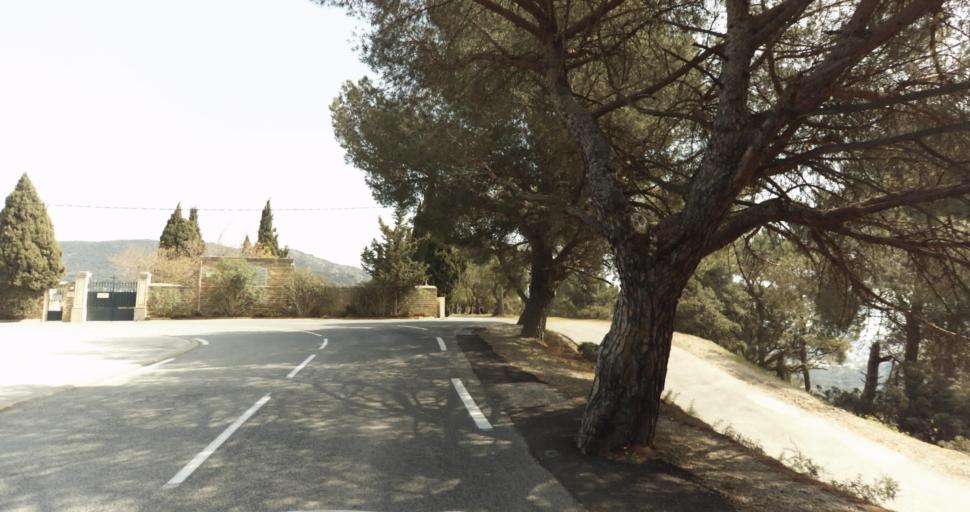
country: FR
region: Provence-Alpes-Cote d'Azur
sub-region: Departement du Var
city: Bormes-les-Mimosas
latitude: 43.1555
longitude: 6.3468
